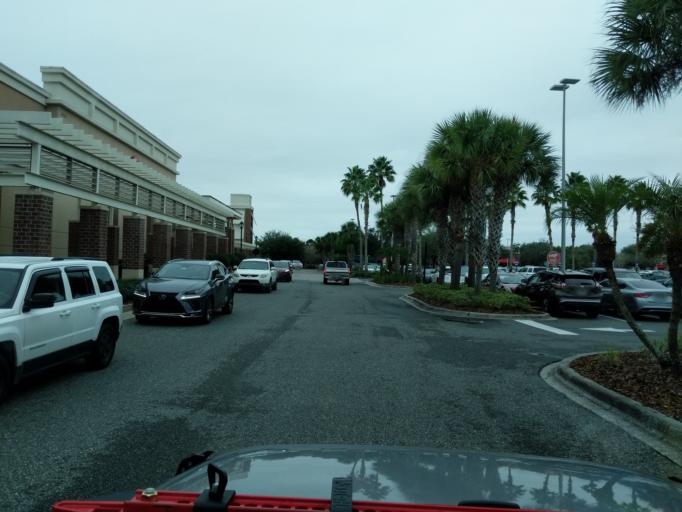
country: US
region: Florida
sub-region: Orange County
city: Winter Garden
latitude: 28.5212
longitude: -81.5851
